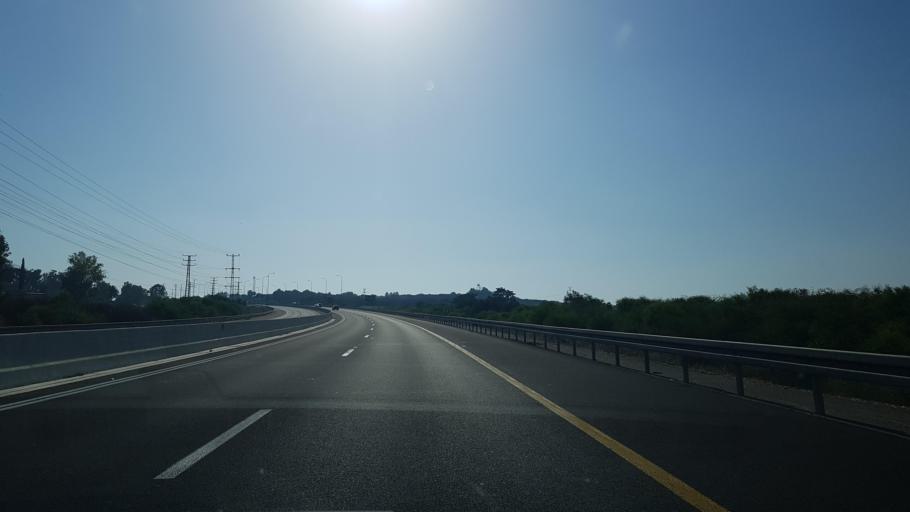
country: IL
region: Southern District
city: Ashqelon
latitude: 31.6889
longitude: 34.6728
